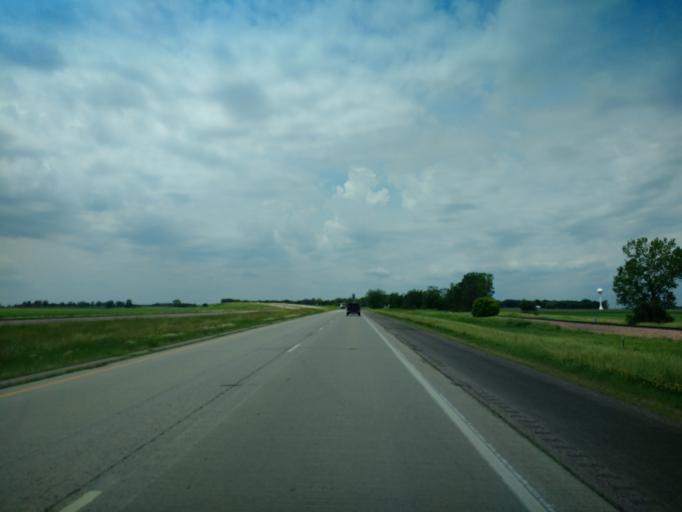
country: US
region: Minnesota
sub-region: Watonwan County
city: Saint James
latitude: 43.9607
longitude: -94.7710
